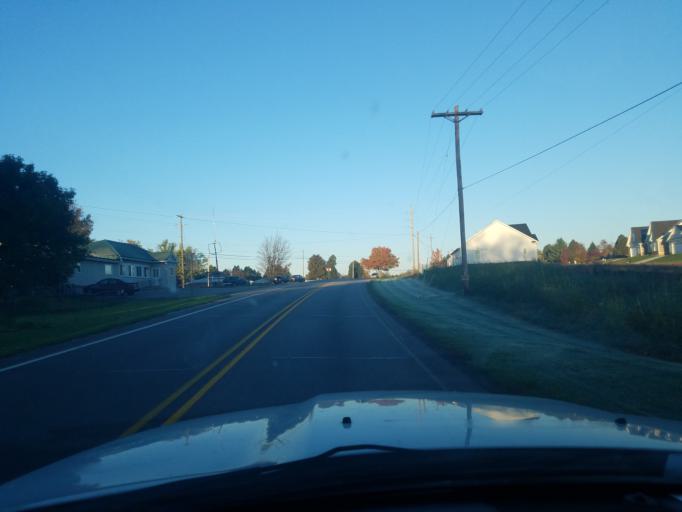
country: US
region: Indiana
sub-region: Floyd County
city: Galena
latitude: 38.3674
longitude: -85.9727
